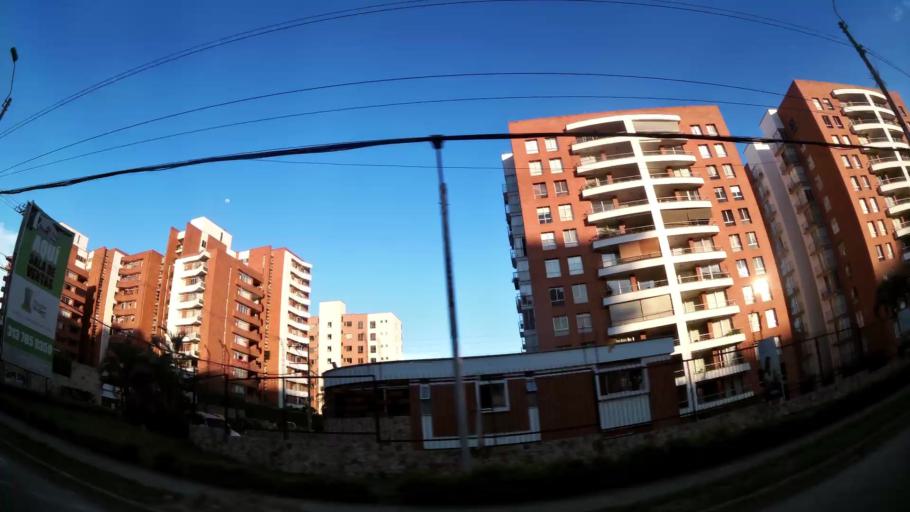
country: CO
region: Valle del Cauca
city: Cali
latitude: 3.4306
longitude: -76.5513
